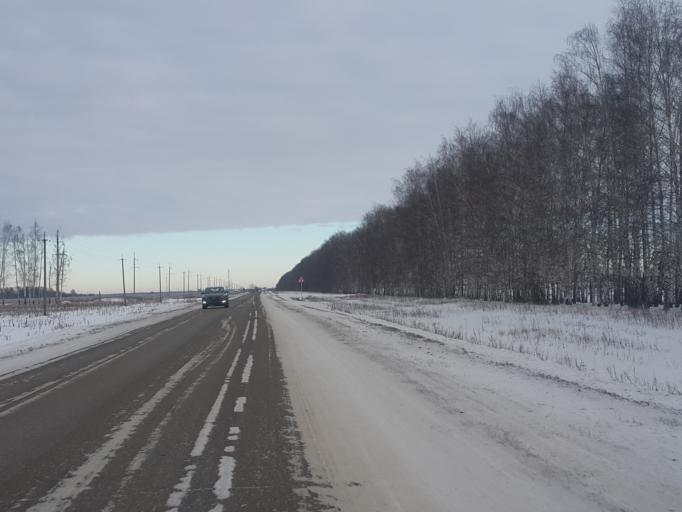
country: RU
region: Tambov
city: Novaya Lyada
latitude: 52.8090
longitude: 41.7888
